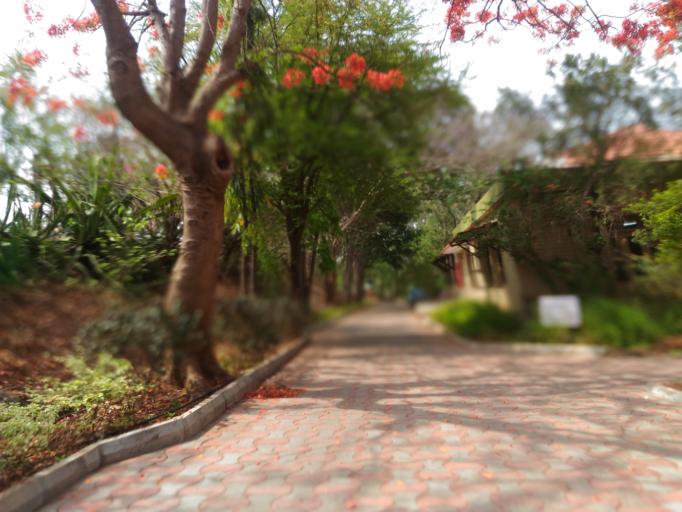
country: IN
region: Karnataka
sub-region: Bangalore Urban
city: Bangalore
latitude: 12.8538
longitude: 77.5103
